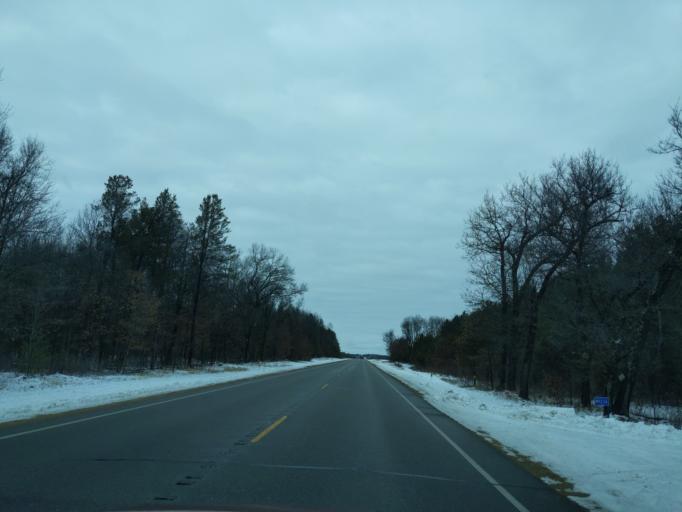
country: US
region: Wisconsin
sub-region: Waushara County
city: Wautoma
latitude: 43.9721
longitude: -89.3276
